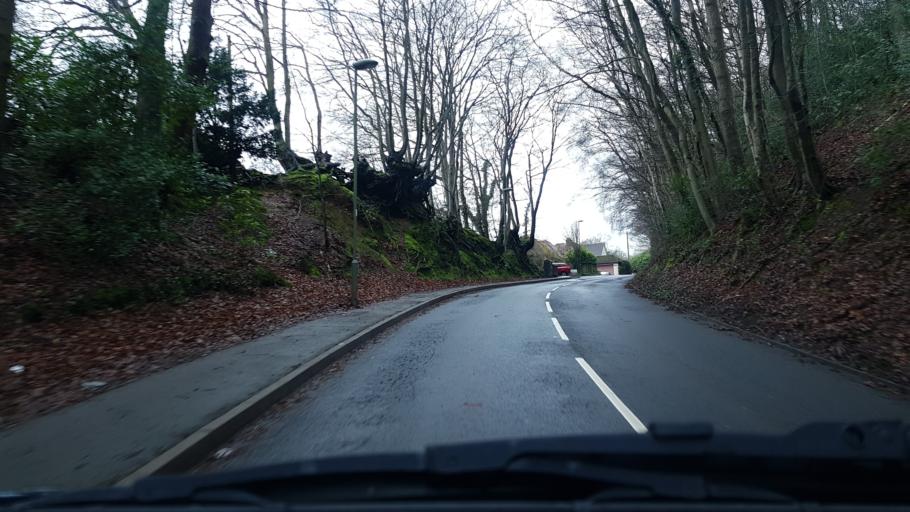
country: GB
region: England
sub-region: Surrey
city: Hindhead
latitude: 51.0891
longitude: -0.7454
